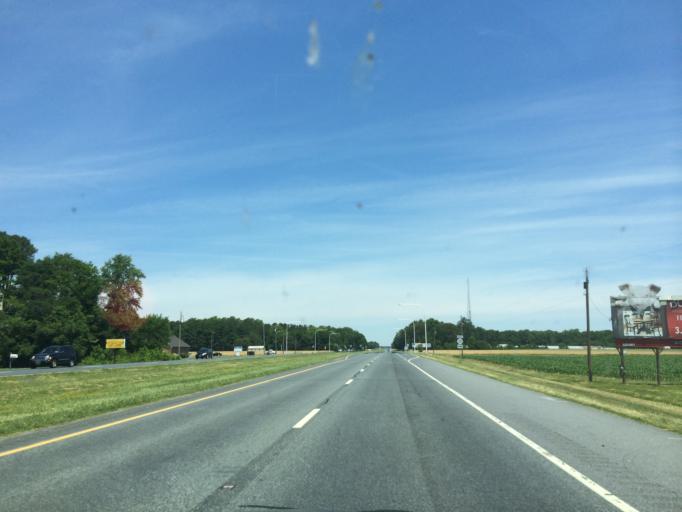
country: US
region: Delaware
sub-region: Sussex County
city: Delmar
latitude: 38.4996
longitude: -75.5572
